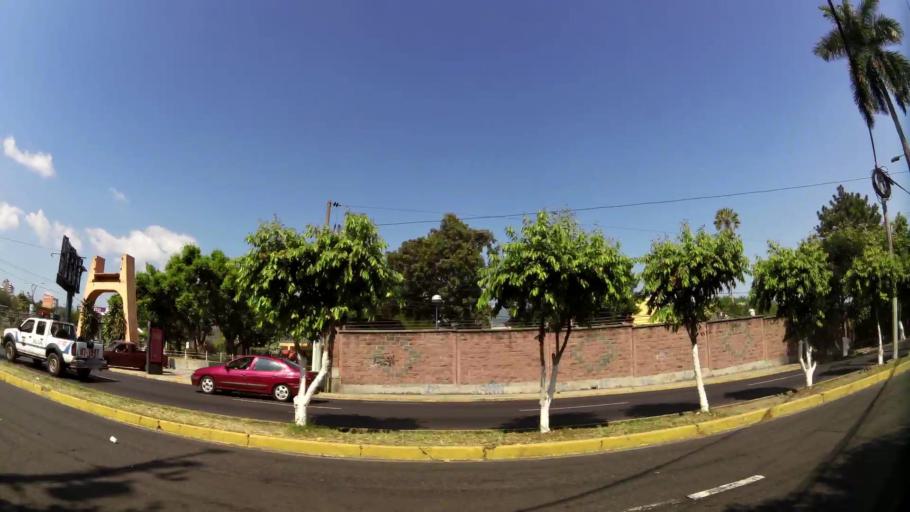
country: SV
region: La Libertad
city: Antiguo Cuscatlan
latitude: 13.6867
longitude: -89.2365
